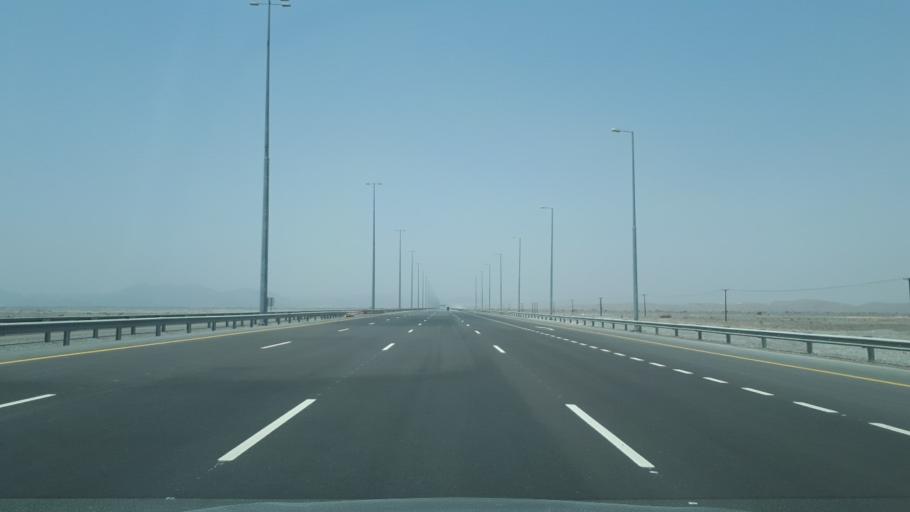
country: OM
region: Al Batinah
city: Barka'
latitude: 23.5540
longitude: 57.6893
